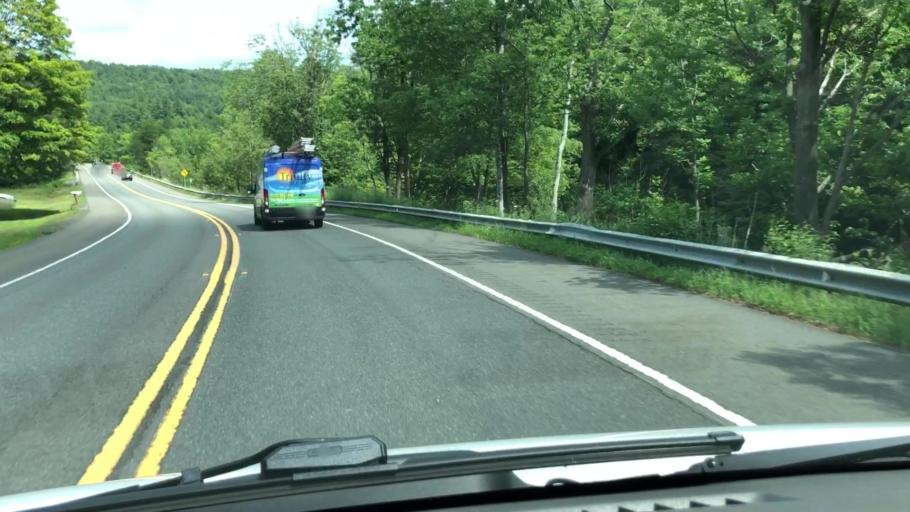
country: US
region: Massachusetts
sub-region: Hampshire County
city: Chesterfield
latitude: 42.4401
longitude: -72.8664
